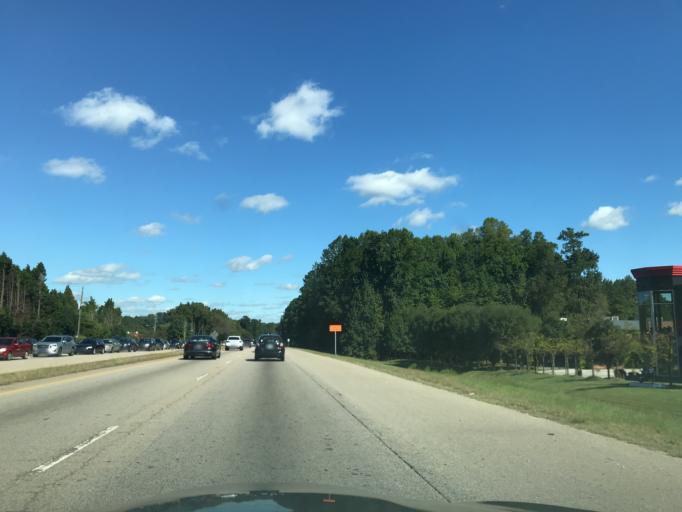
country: US
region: North Carolina
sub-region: Wake County
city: Wake Forest
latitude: 35.8994
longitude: -78.5582
